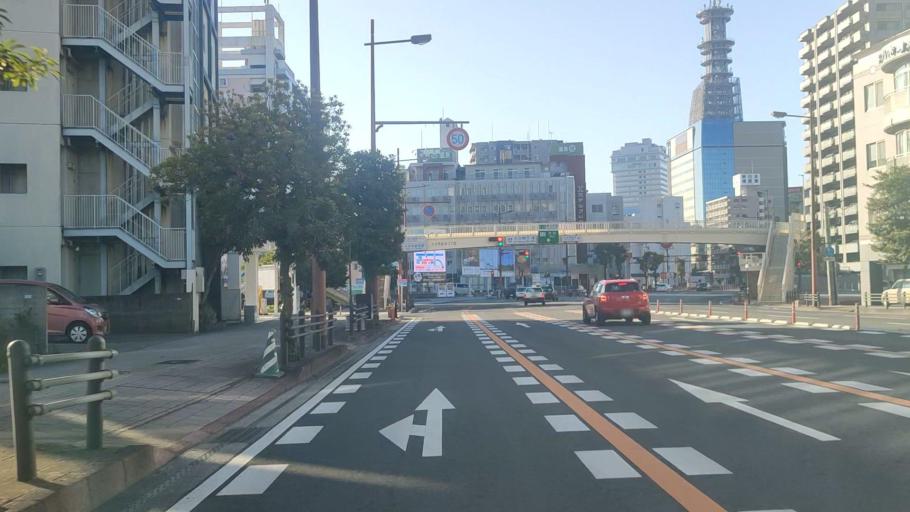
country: JP
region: Oita
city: Oita
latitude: 33.2320
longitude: 131.6131
